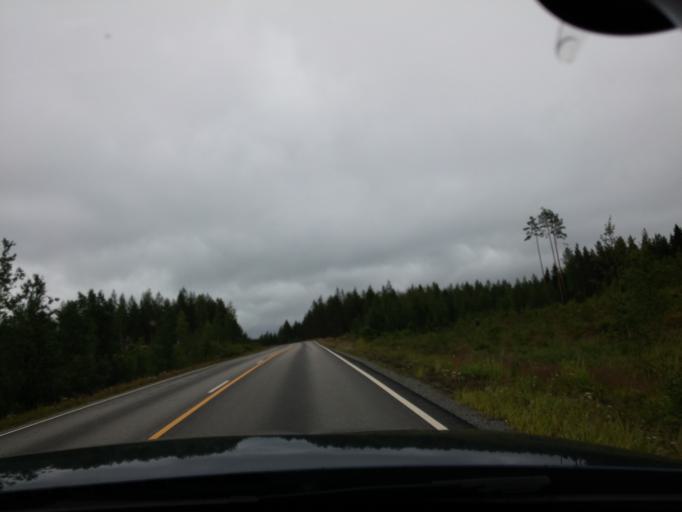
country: FI
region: Central Finland
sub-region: Saarijaervi-Viitasaari
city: Pylkoenmaeki
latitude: 62.6406
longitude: 24.8492
